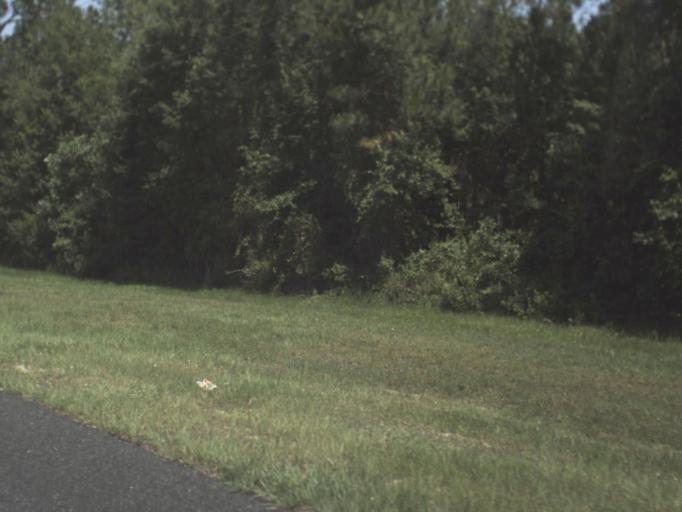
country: US
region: Florida
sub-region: Alachua County
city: Hawthorne
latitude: 29.5991
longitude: -82.1685
